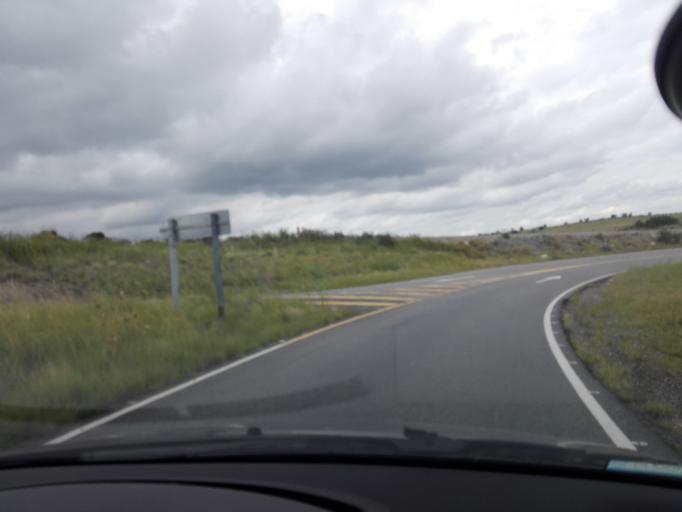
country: AR
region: Cordoba
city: Cuesta Blanca
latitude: -31.5689
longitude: -64.5887
